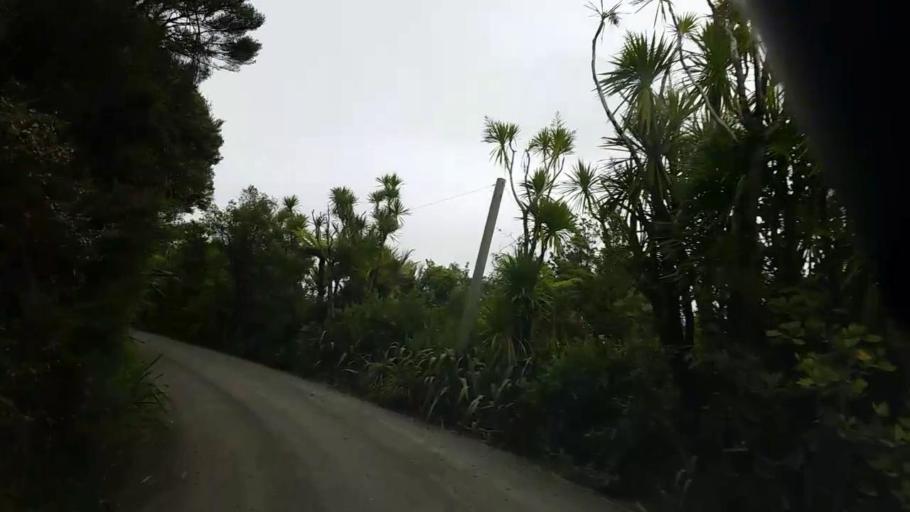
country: NZ
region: Auckland
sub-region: Auckland
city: Muriwai Beach
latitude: -36.9251
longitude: 174.4935
